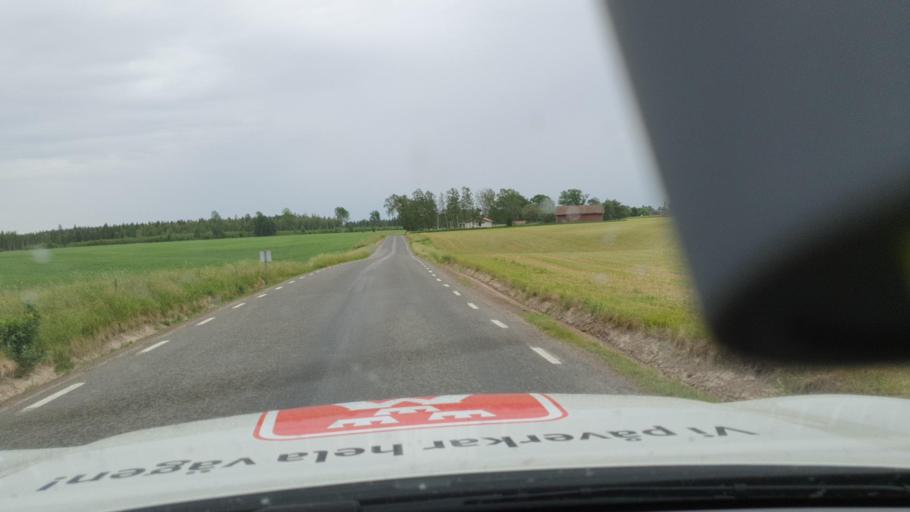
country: SE
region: Vaestra Goetaland
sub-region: Tidaholms Kommun
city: Olofstorp
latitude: 58.3280
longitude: 14.0596
